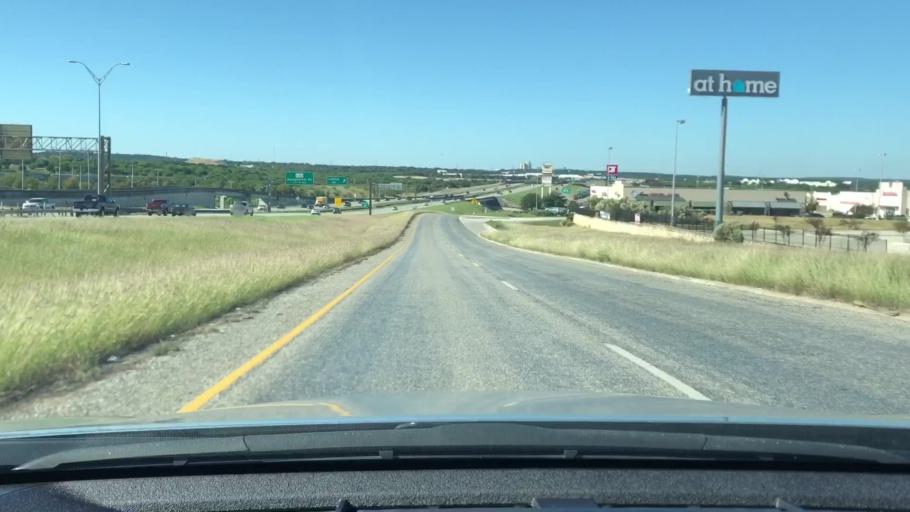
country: US
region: Texas
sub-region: Bexar County
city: Live Oak
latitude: 29.5750
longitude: -98.3386
